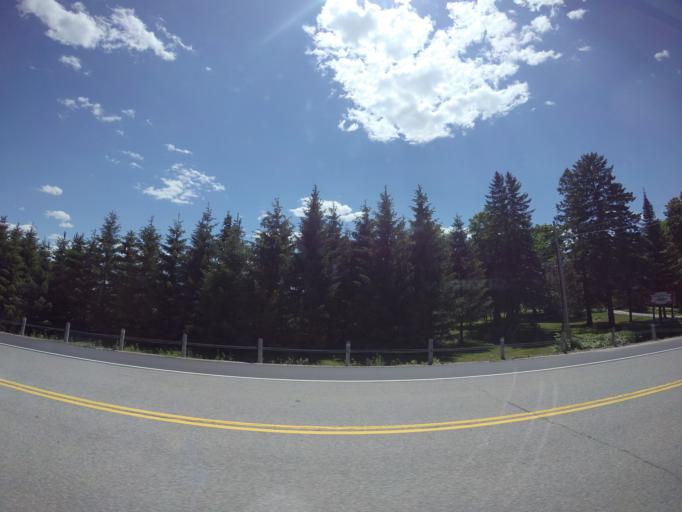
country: CA
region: Ontario
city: Carleton Place
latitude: 45.1324
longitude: -76.1914
